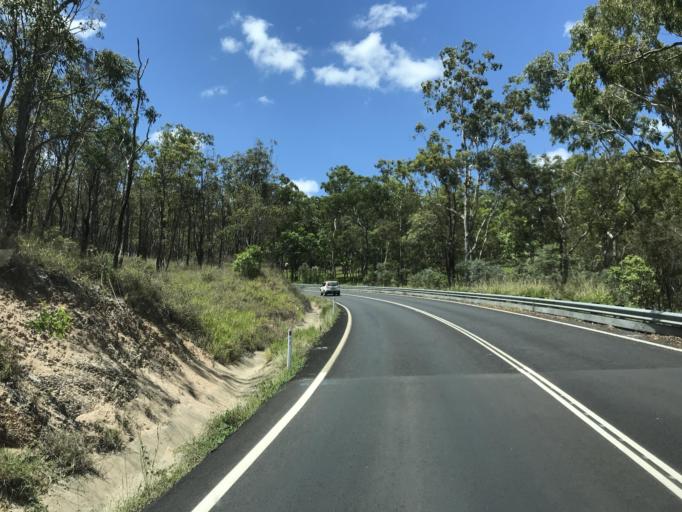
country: AU
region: Queensland
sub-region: Tablelands
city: Atherton
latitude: -17.3991
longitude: 145.3901
